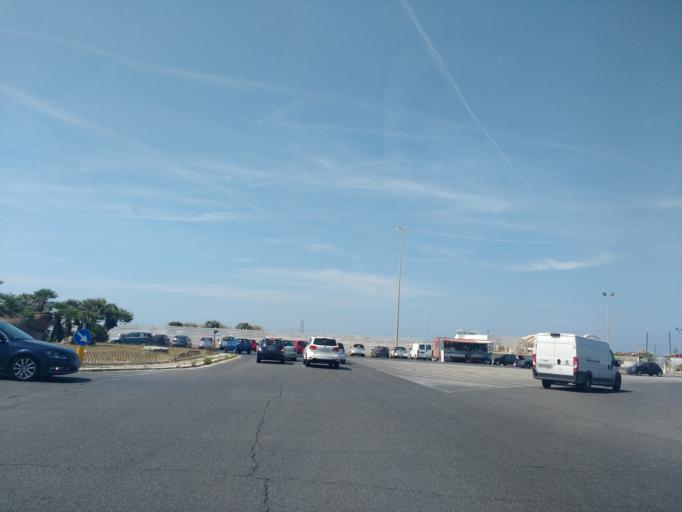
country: IT
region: Latium
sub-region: Citta metropolitana di Roma Capitale
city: Lido di Ostia
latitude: 41.7150
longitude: 12.3177
